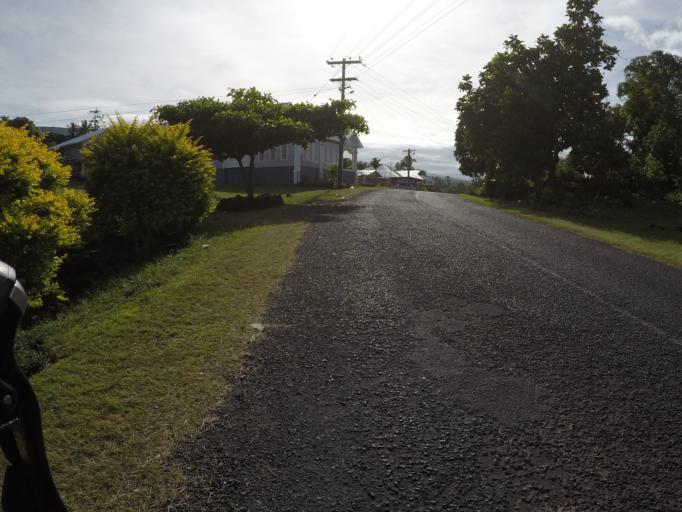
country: WS
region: Vaisigano
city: Asau
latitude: -13.6784
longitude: -172.6316
